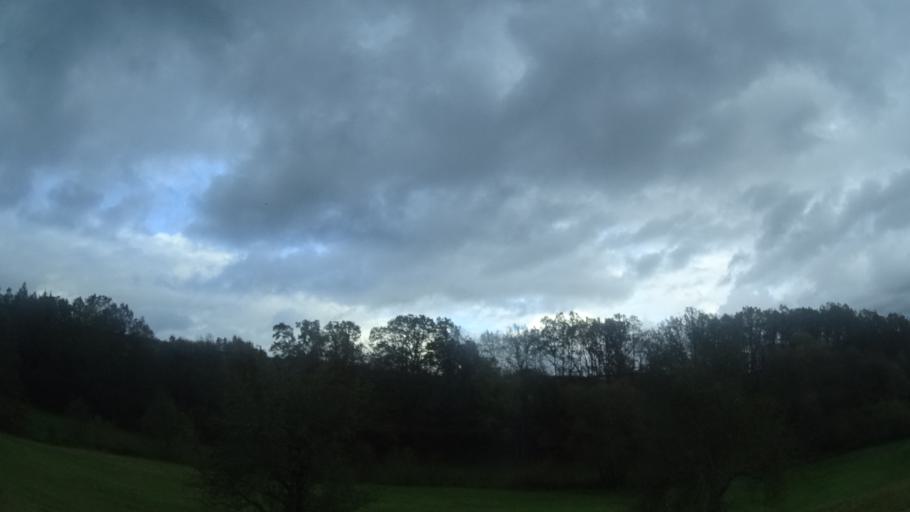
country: DE
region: Bavaria
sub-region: Regierungsbezirk Unterfranken
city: Hohenroth
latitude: 50.3536
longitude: 10.1233
